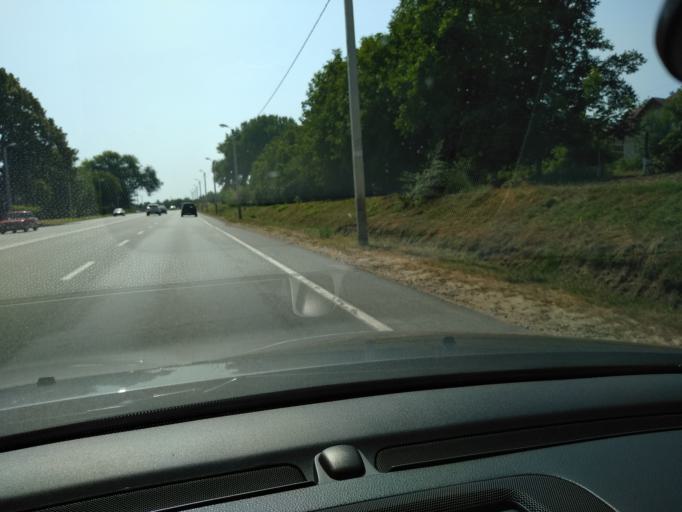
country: MD
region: Chisinau
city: Cricova
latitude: 47.2356
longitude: 28.7619
